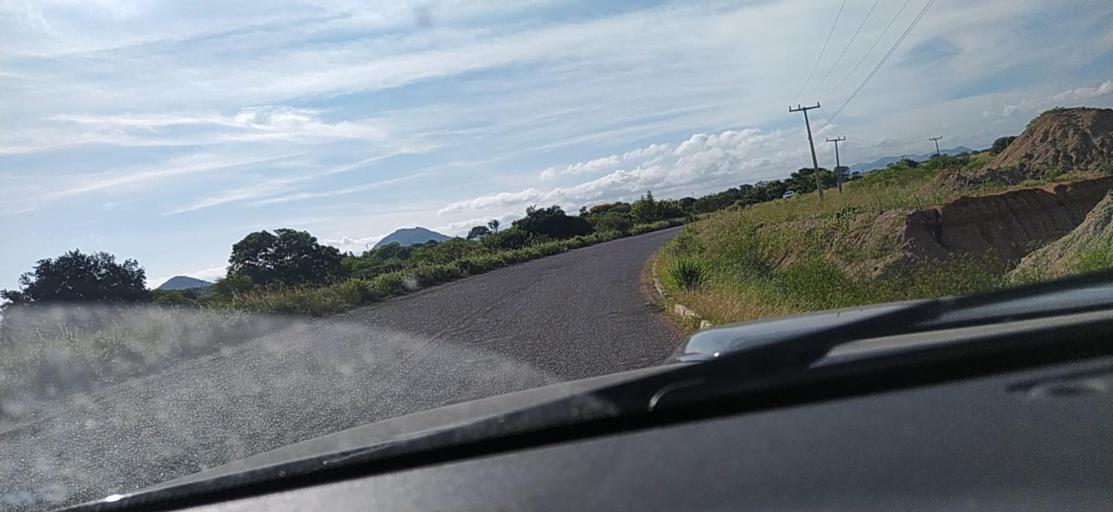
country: BR
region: Bahia
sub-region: Guanambi
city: Guanambi
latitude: -14.1499
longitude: -42.8284
